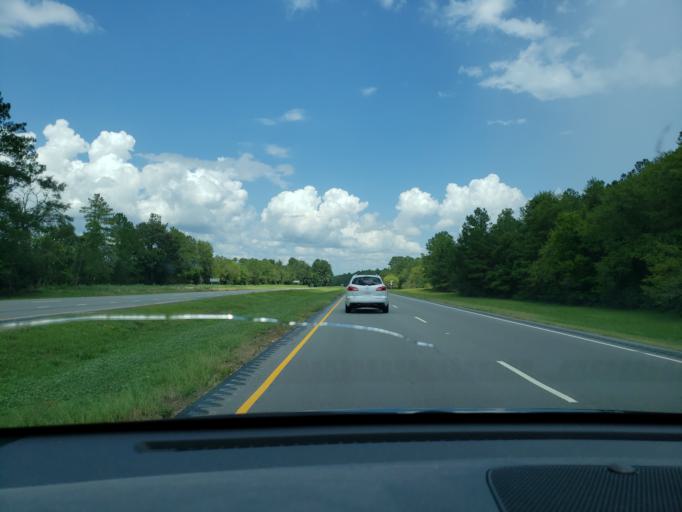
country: US
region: North Carolina
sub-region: Robeson County
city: Saint Pauls
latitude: 34.8471
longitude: -78.8537
